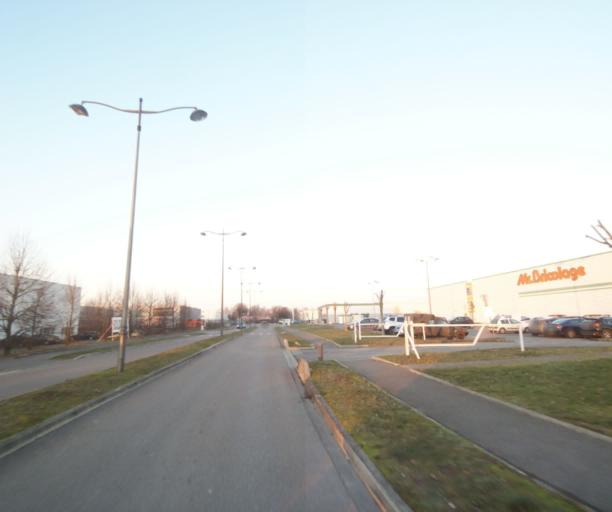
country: FR
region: Champagne-Ardenne
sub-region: Departement de la Haute-Marne
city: Saint-Dizier
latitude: 48.6240
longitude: 4.9648
